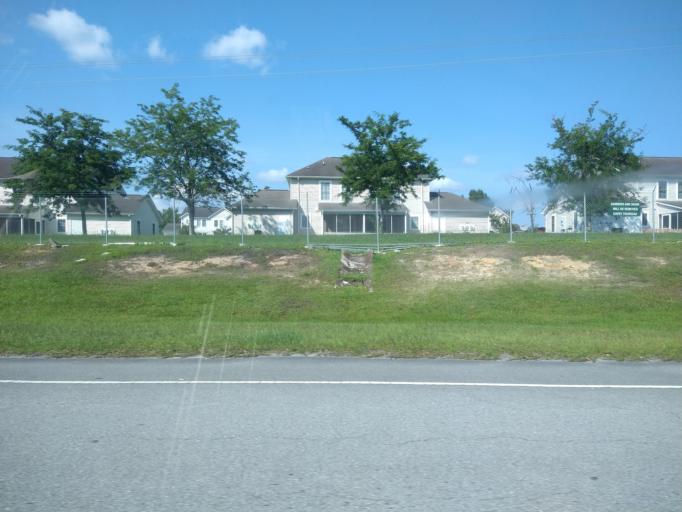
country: US
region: North Carolina
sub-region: Onslow County
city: Piney Green
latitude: 34.7321
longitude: -77.3500
